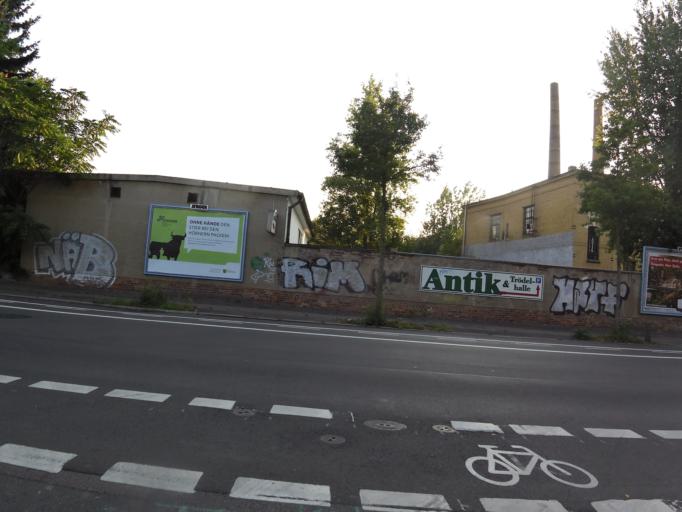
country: DE
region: Saxony
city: Leipzig
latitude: 51.3320
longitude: 12.3080
